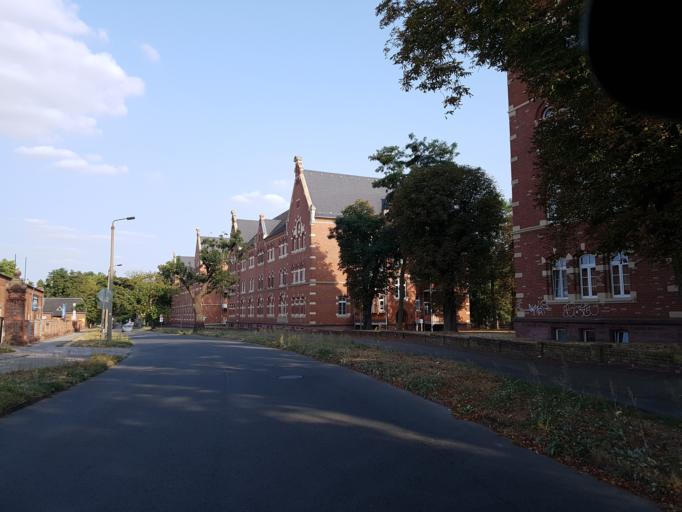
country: DE
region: Saxony
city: Torgau
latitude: 51.5626
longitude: 12.9789
